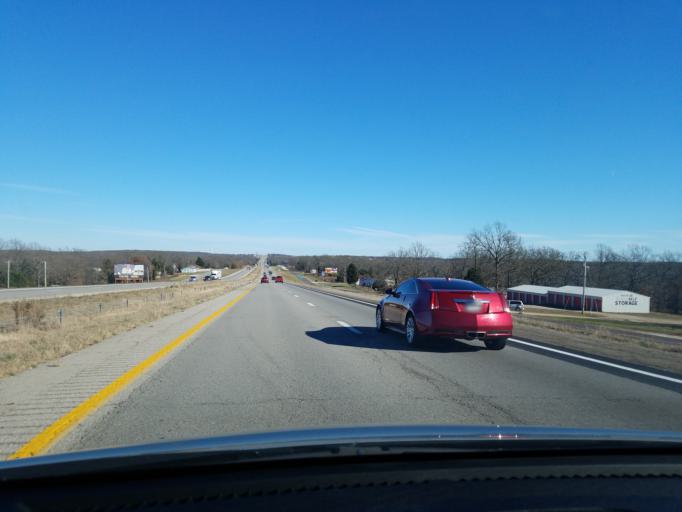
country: US
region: Missouri
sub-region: Pulaski County
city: Richland
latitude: 37.7794
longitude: -92.3119
